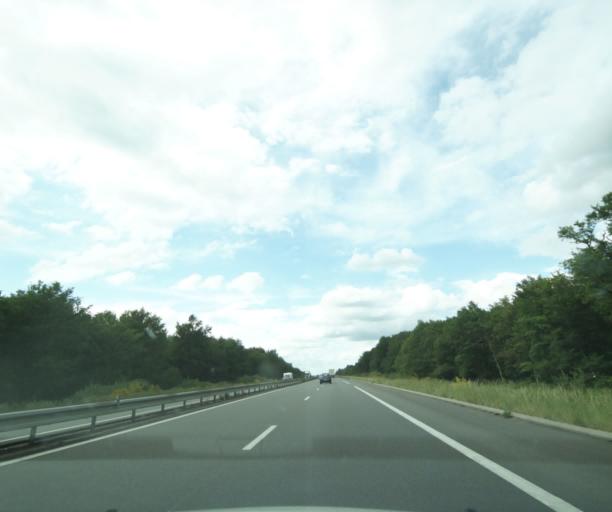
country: FR
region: Centre
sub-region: Departement du Loir-et-Cher
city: Salbris
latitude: 47.4310
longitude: 2.0151
